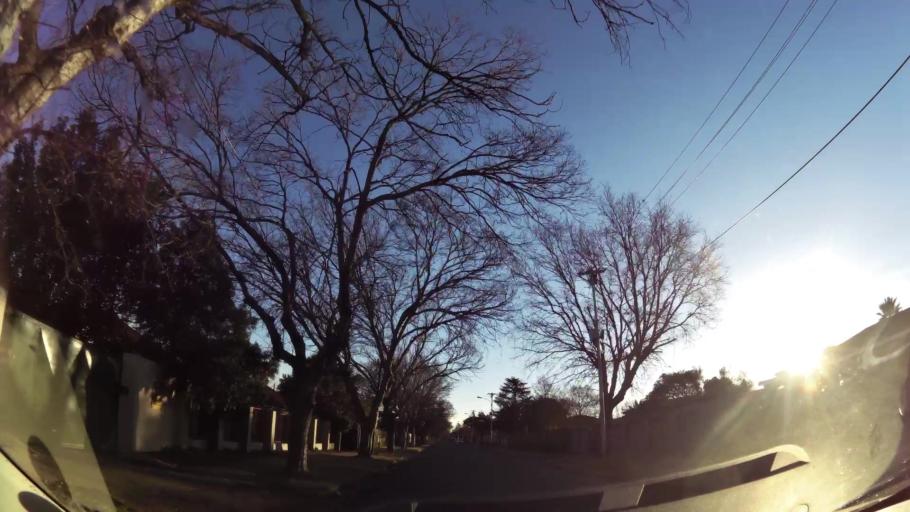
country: ZA
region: Gauteng
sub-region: City of Johannesburg Metropolitan Municipality
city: Roodepoort
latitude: -26.1746
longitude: 27.9326
